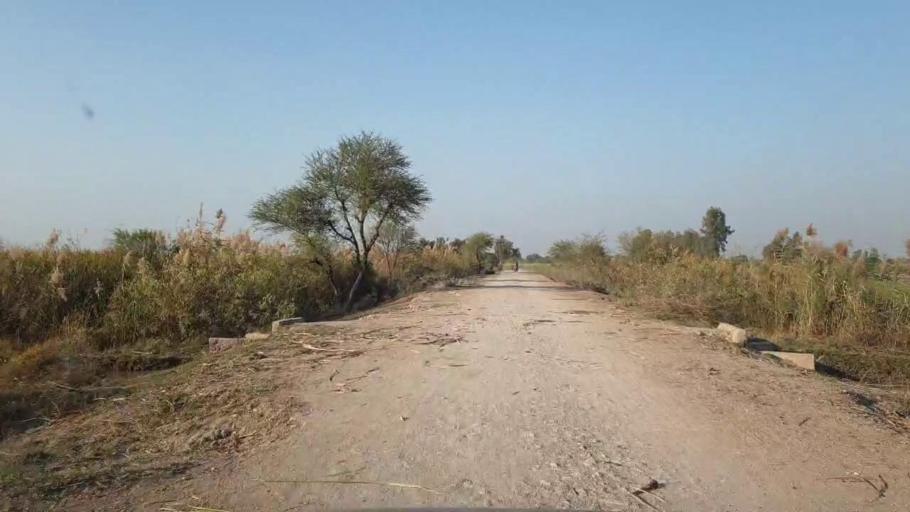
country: PK
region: Sindh
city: Tando Allahyar
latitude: 25.3486
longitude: 68.7059
